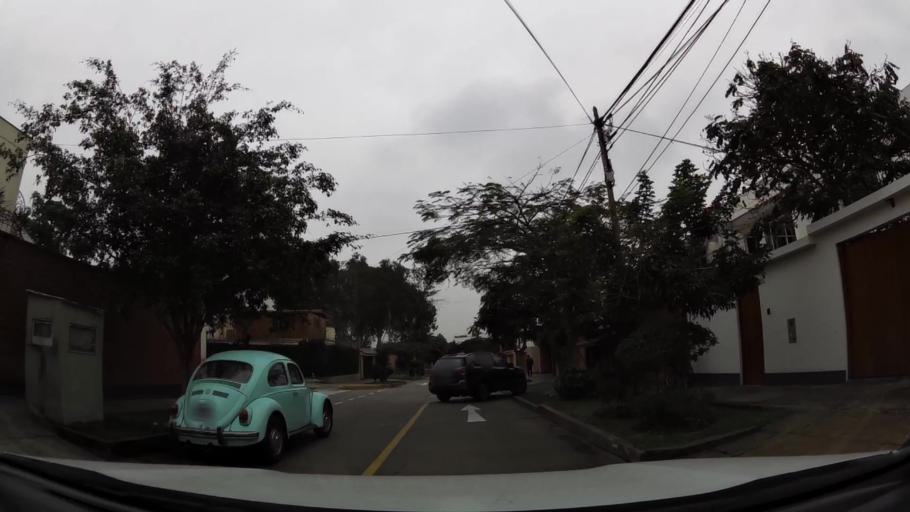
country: PE
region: Lima
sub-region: Lima
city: Surco
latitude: -12.1308
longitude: -77.0087
